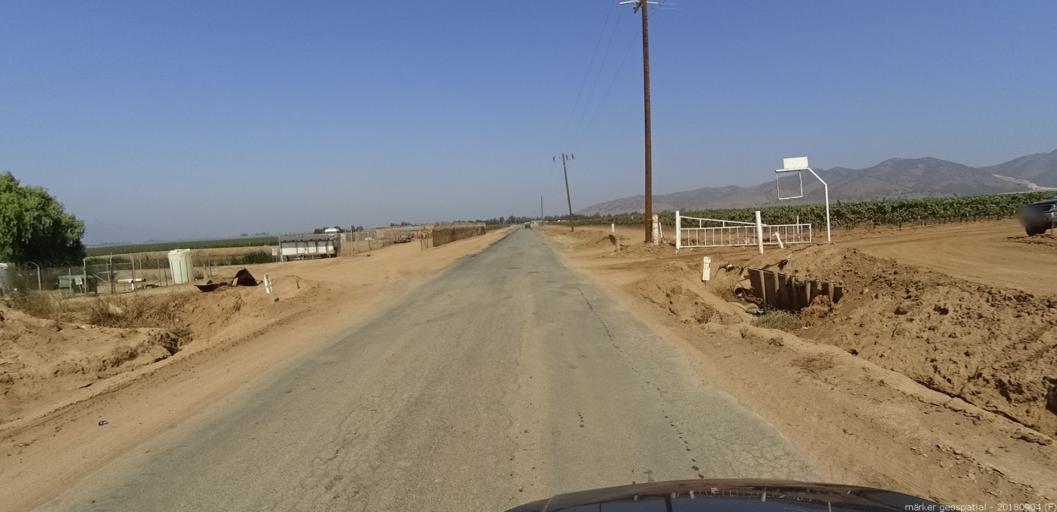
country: US
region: California
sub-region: Monterey County
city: Gonzales
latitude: 36.5434
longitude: -121.4300
